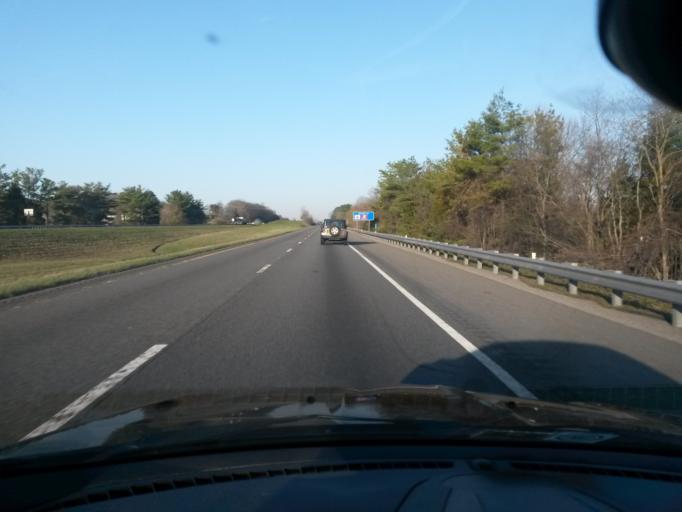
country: US
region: Virginia
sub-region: Montgomery County
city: Christiansburg
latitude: 37.1205
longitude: -80.4058
